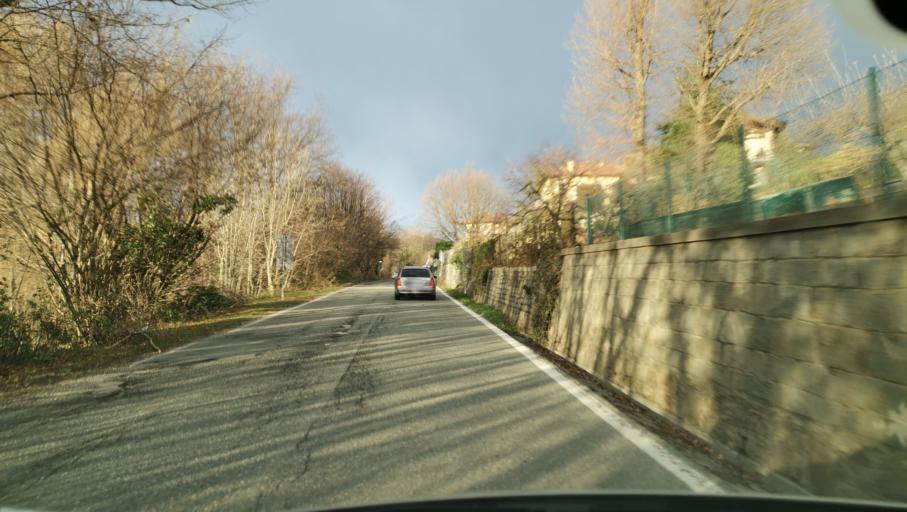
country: IT
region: Piedmont
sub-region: Provincia di Torino
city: Giaveno
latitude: 45.0509
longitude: 7.3280
